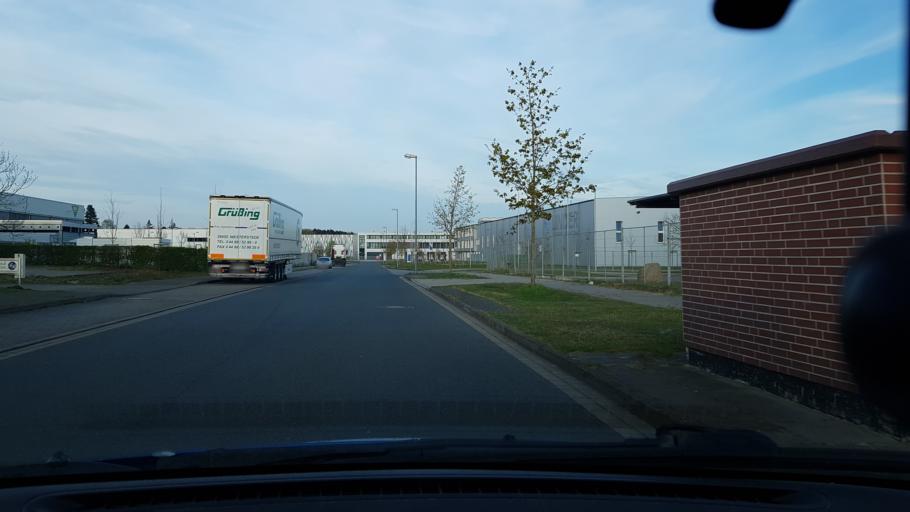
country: DE
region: Lower Saxony
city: Drestedt
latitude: 53.3251
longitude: 9.8135
